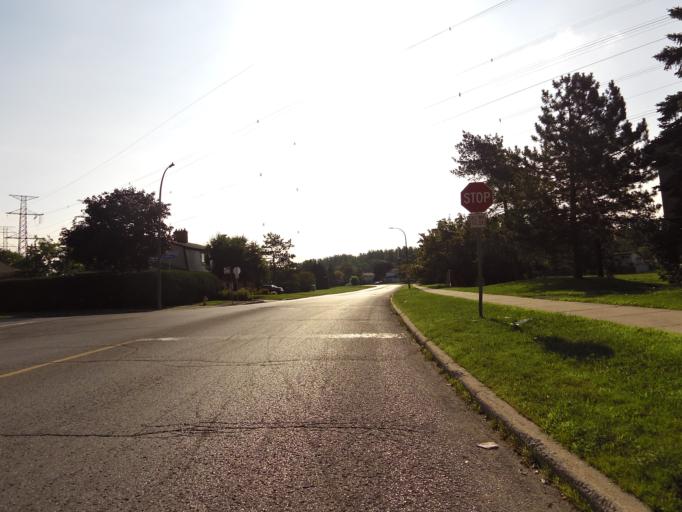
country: CA
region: Ontario
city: Ottawa
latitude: 45.3346
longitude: -75.7403
